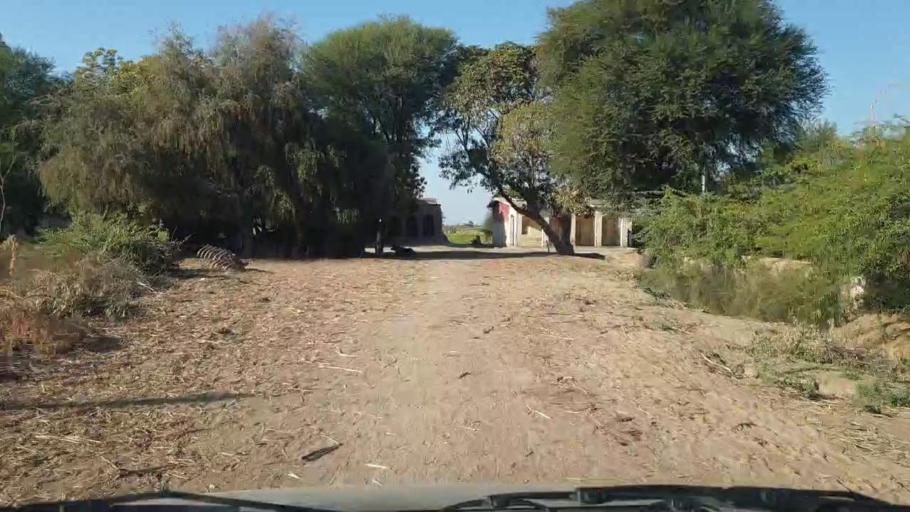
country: PK
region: Sindh
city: Samaro
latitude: 25.3666
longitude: 69.2902
